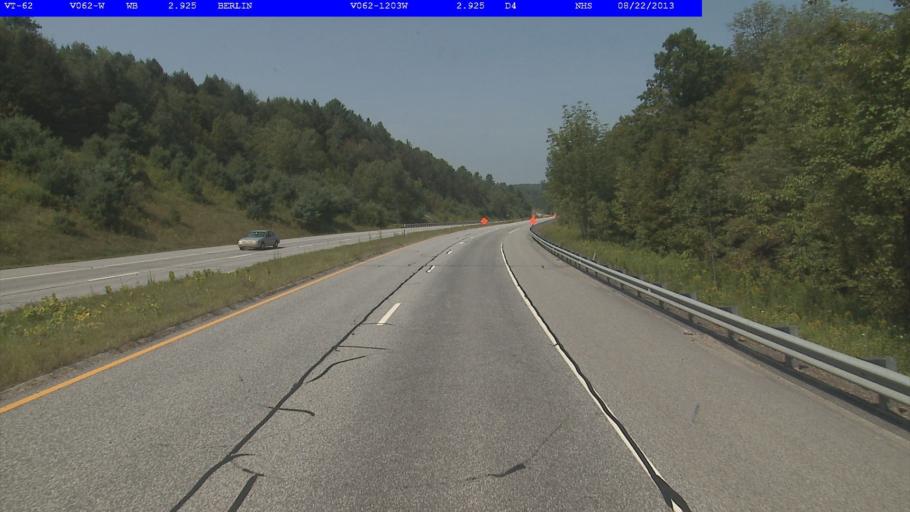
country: US
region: Vermont
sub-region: Washington County
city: Barre
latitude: 44.2128
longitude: -72.5344
